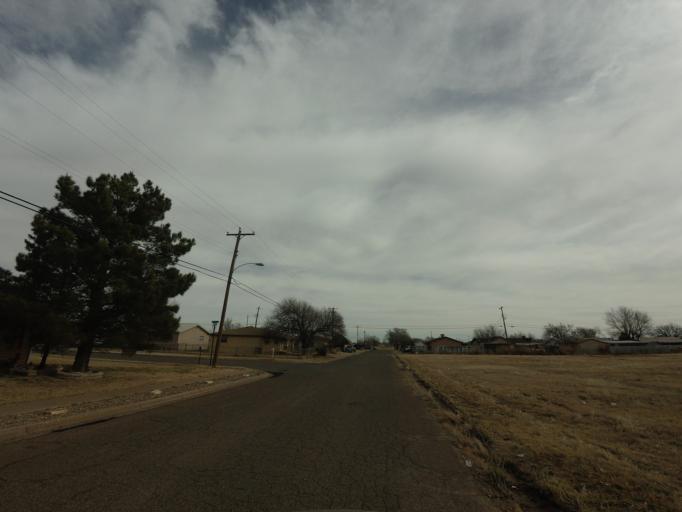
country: US
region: New Mexico
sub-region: Curry County
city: Clovis
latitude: 34.4067
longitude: -103.2388
